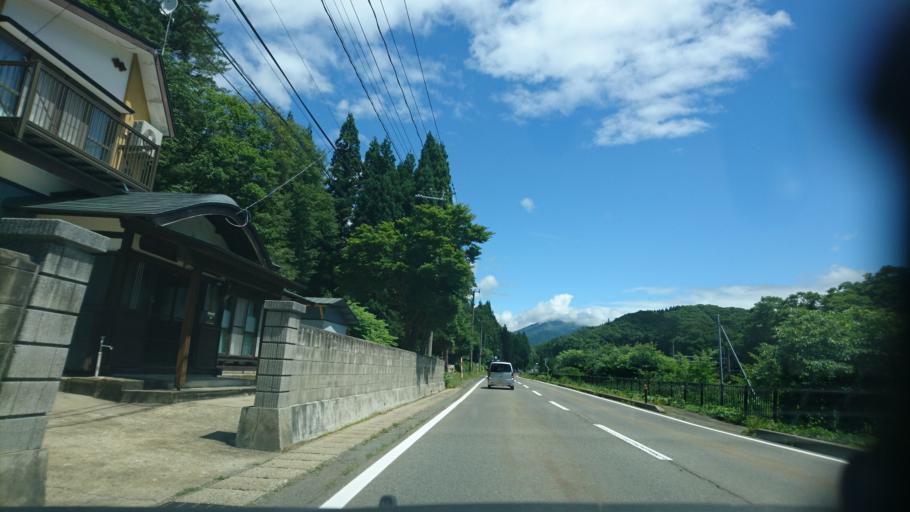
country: JP
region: Akita
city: Kakunodatemachi
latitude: 39.6703
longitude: 140.6932
